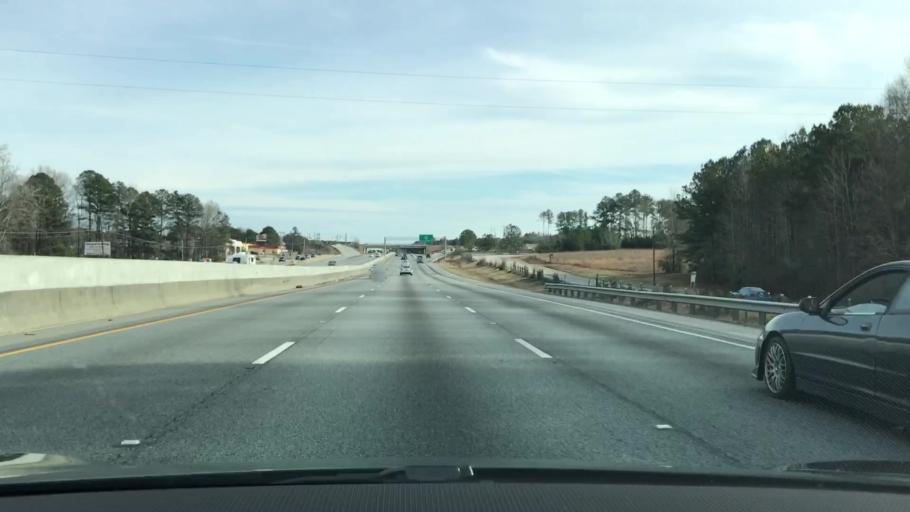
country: US
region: Georgia
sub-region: Rockdale County
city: Conyers
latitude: 33.6398
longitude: -83.9843
